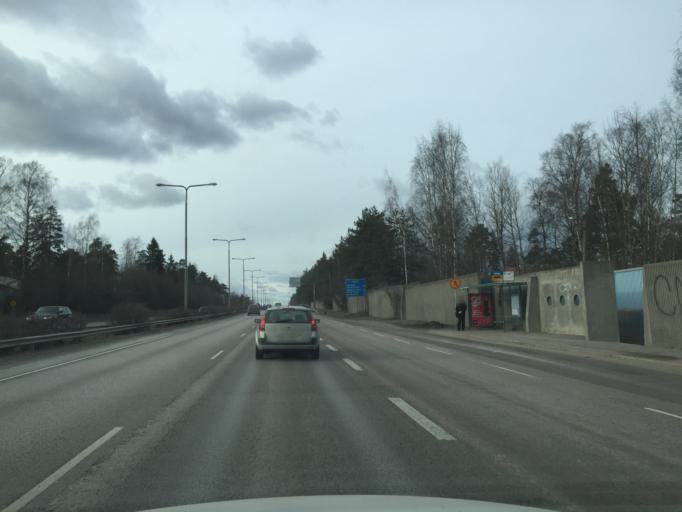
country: FI
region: Uusimaa
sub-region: Helsinki
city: Teekkarikylae
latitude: 60.2410
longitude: 24.8947
